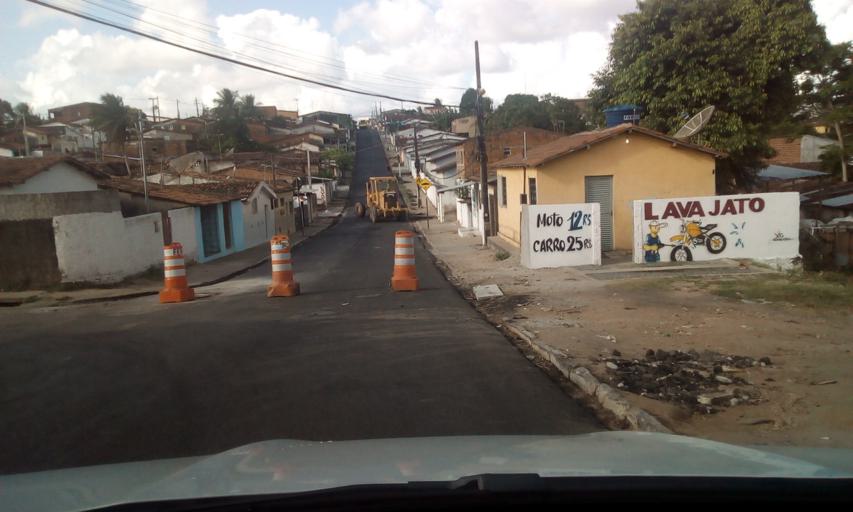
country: BR
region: Paraiba
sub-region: Conde
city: Conde
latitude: -7.1912
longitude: -34.8843
